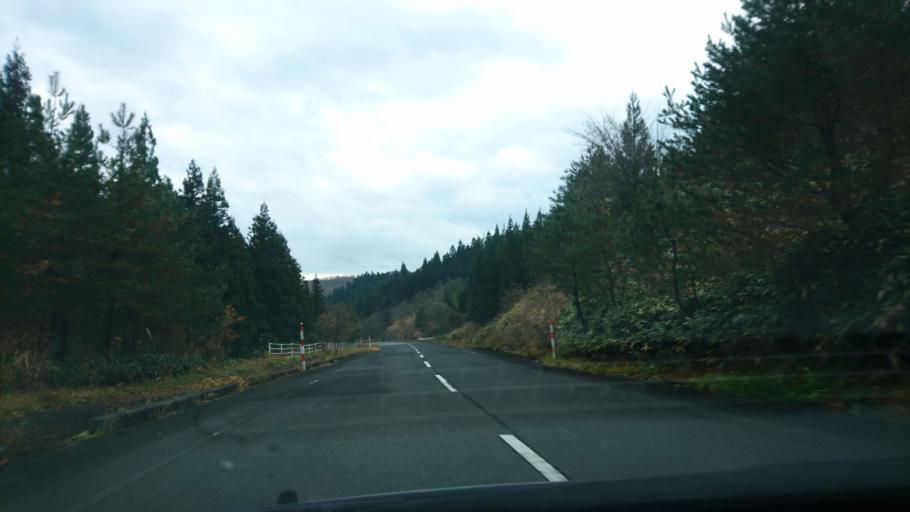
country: JP
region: Iwate
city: Ichinoseki
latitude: 38.9187
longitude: 140.9083
